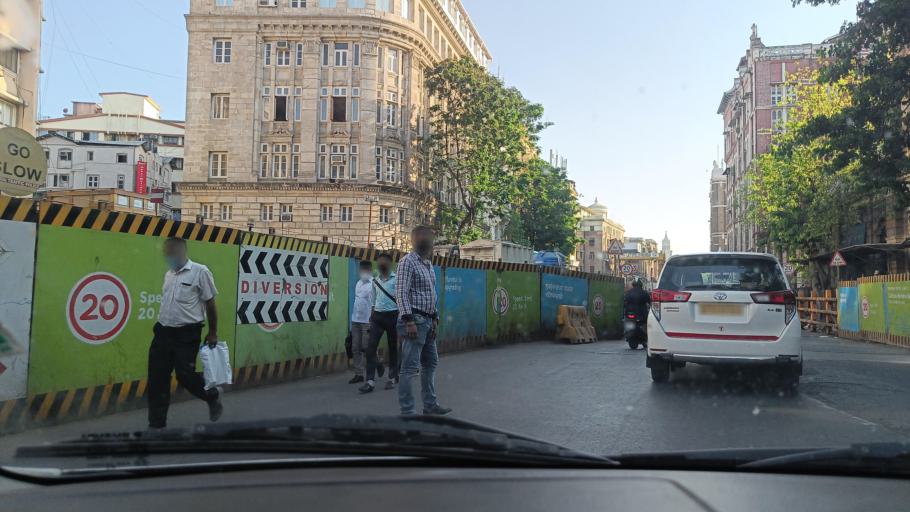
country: IN
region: Maharashtra
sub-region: Raigarh
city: Uran
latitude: 18.9364
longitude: 72.8338
